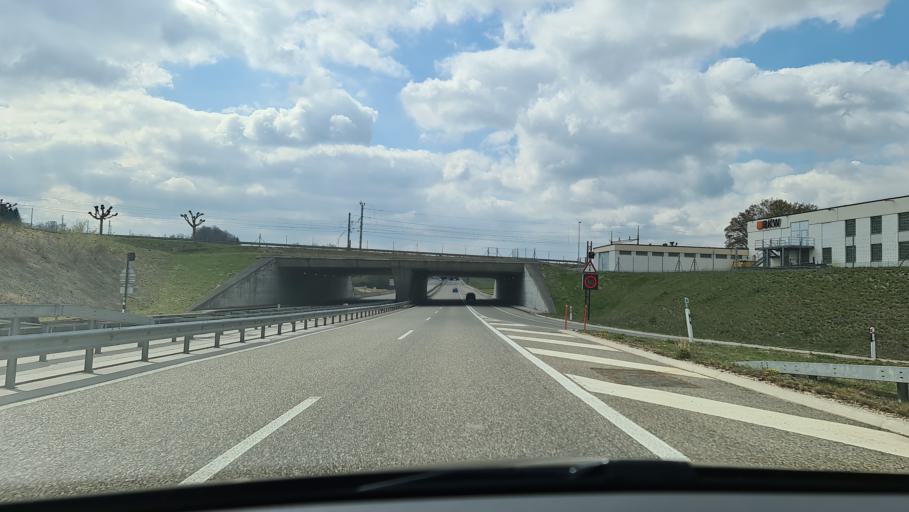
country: CH
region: Jura
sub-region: Delemont District
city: Courroux
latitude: 47.3516
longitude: 7.3671
